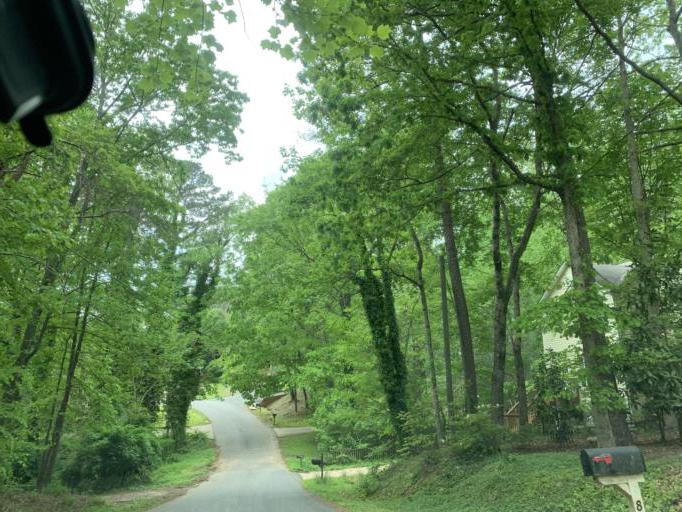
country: US
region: Georgia
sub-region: Forsyth County
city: Cumming
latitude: 34.1937
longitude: -84.1181
